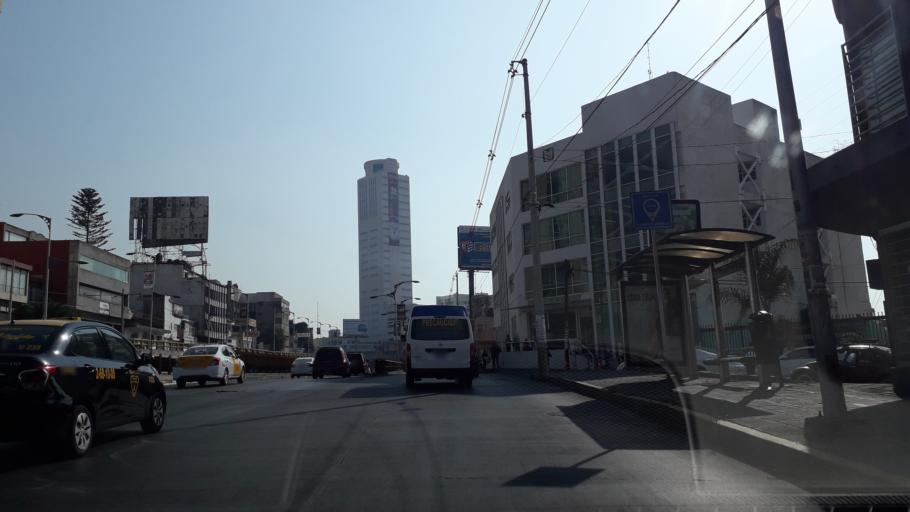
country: MX
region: Puebla
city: Puebla
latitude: 19.0517
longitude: -98.2255
